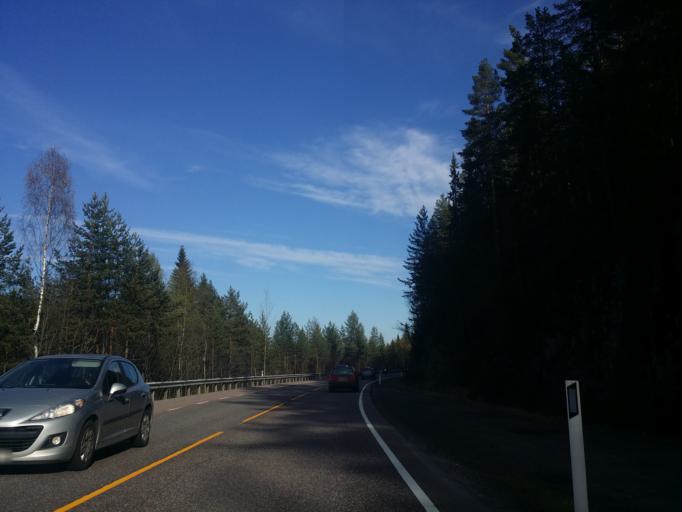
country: NO
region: Buskerud
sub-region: Kongsberg
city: Kongsberg
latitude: 59.6290
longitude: 9.5692
